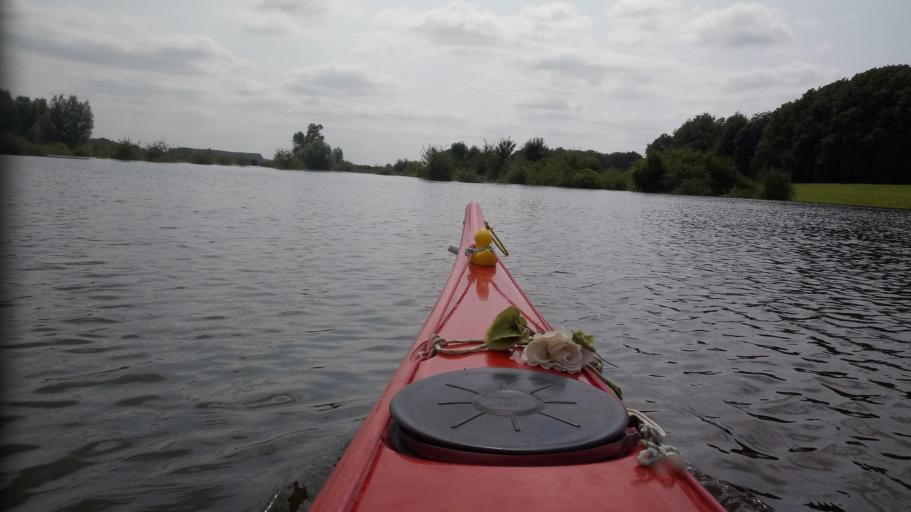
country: NL
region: Gelderland
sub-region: Gemeente Zutphen
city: Zutphen
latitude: 52.1114
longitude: 6.1922
